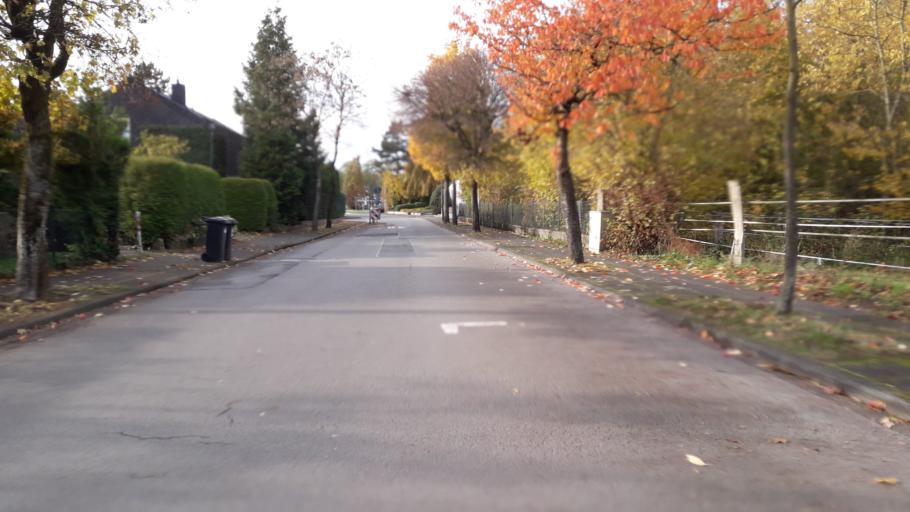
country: DE
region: North Rhine-Westphalia
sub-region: Regierungsbezirk Detmold
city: Schlangen
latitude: 51.7979
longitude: 8.8379
